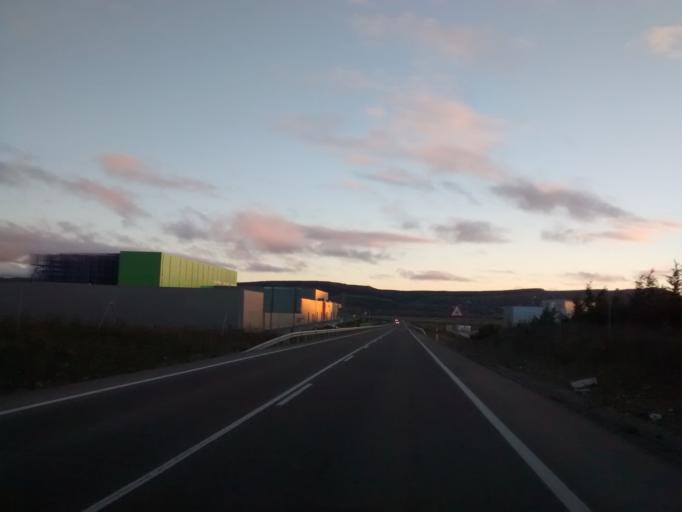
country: ES
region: Castille and Leon
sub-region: Provincia de Palencia
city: Aguilar de Campoo
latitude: 42.7882
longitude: -4.2447
